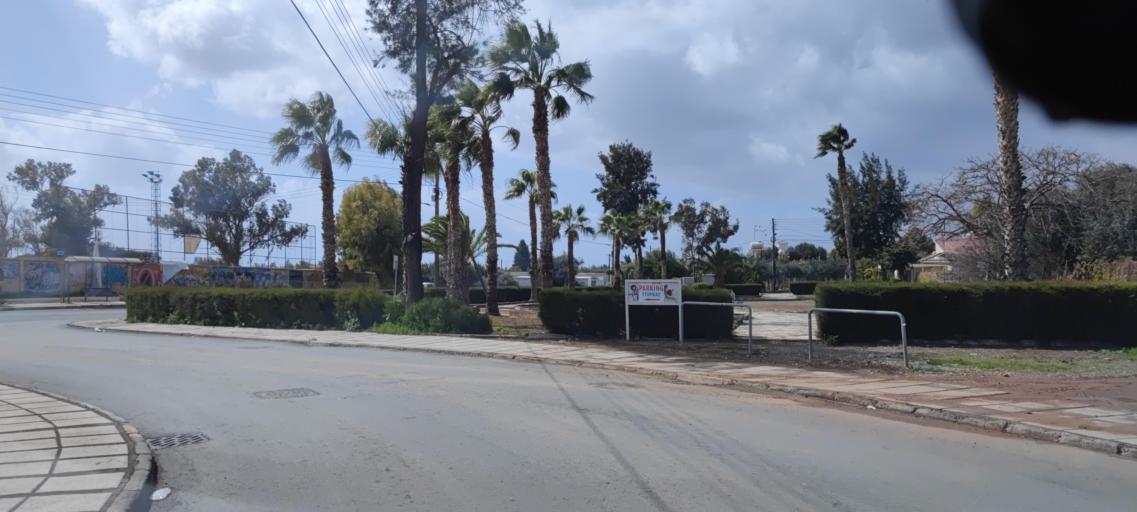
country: CY
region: Limassol
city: Pano Polemidia
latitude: 34.6919
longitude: 32.9931
